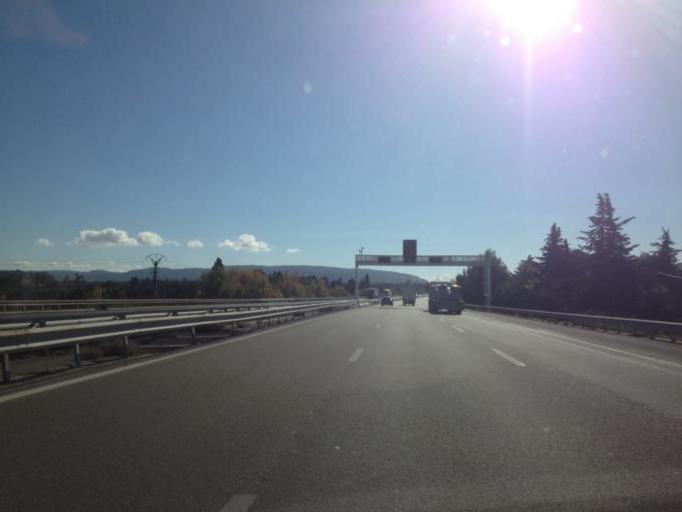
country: FR
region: Provence-Alpes-Cote d'Azur
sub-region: Departement des Bouches-du-Rhone
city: Senas
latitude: 43.7379
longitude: 5.0885
